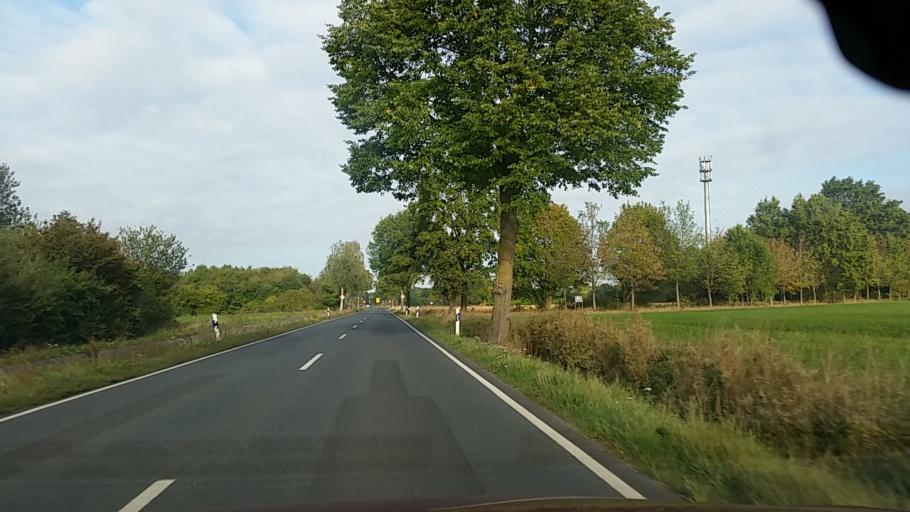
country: DE
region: Lower Saxony
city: Lachendorf
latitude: 52.6182
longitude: 10.2633
